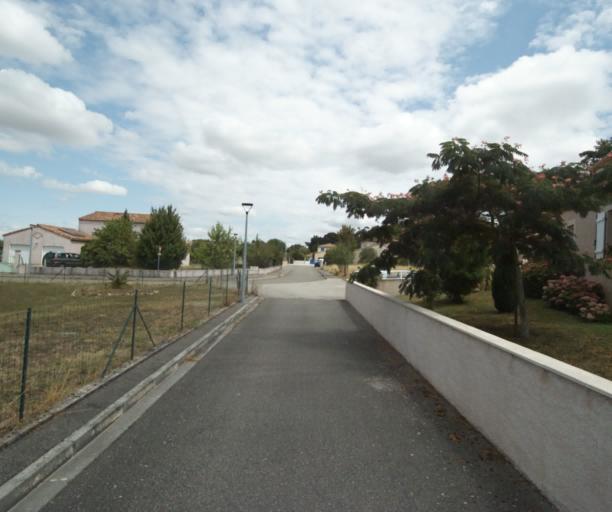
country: FR
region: Midi-Pyrenees
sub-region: Departement de la Haute-Garonne
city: Revel
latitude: 43.4510
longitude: 1.9931
